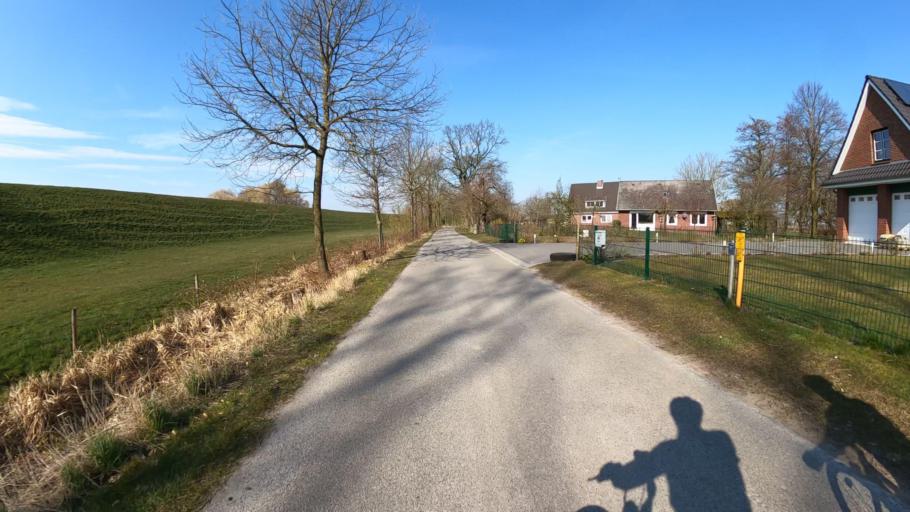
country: DE
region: Schleswig-Holstein
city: Seestermuhe
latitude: 53.6858
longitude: 9.5629
